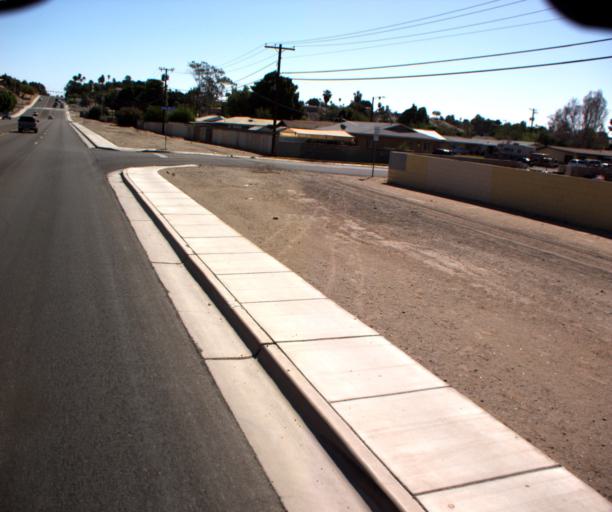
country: US
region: Arizona
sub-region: Yuma County
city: Yuma
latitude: 32.6984
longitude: -114.6454
